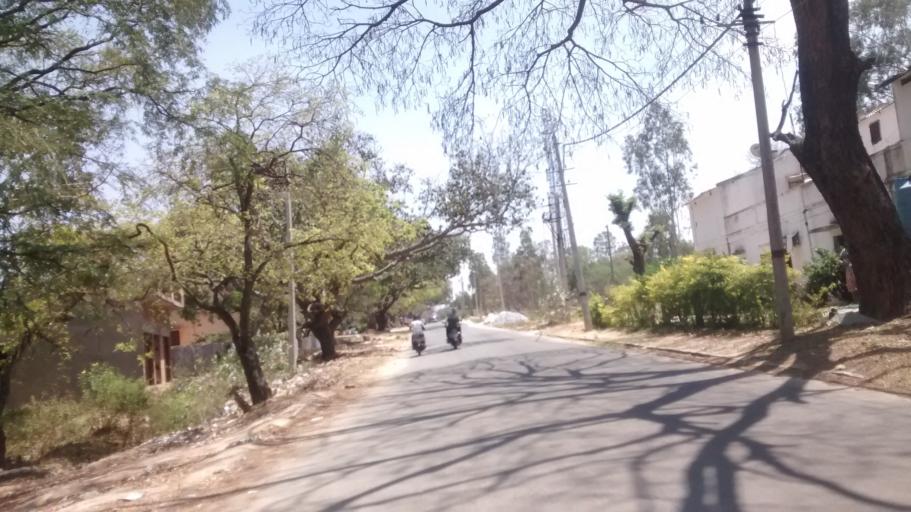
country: IN
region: Karnataka
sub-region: Kolar
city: Robertsonpet
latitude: 13.0286
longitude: 78.3552
